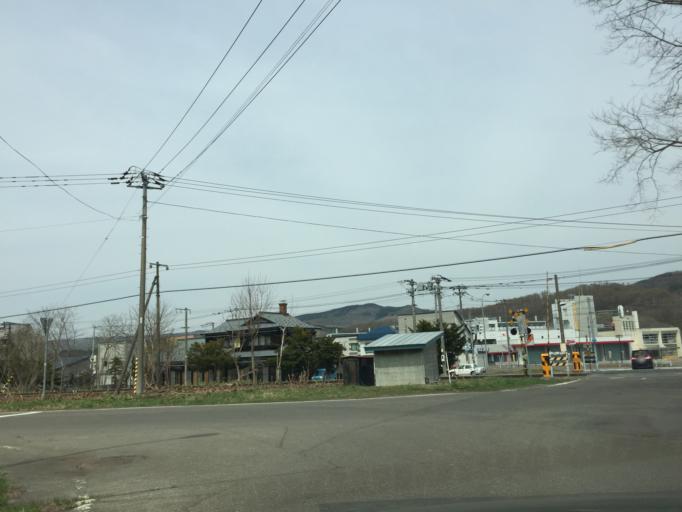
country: JP
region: Hokkaido
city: Akabira
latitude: 43.5514
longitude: 142.0549
